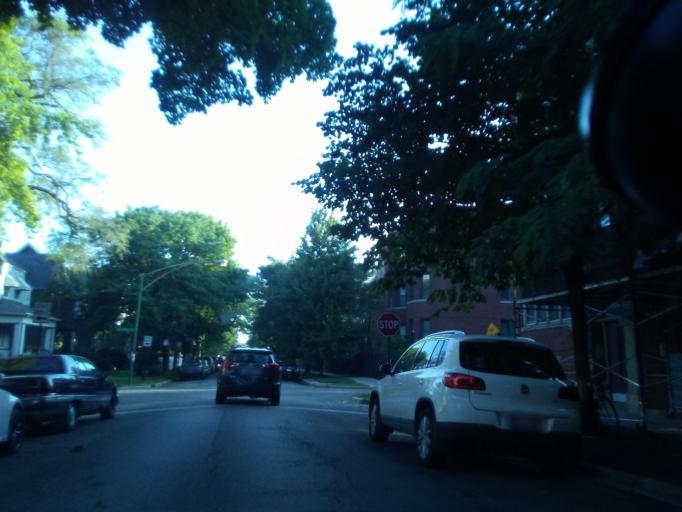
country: US
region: Illinois
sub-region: Cook County
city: Lincolnwood
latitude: 41.9299
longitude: -87.7147
